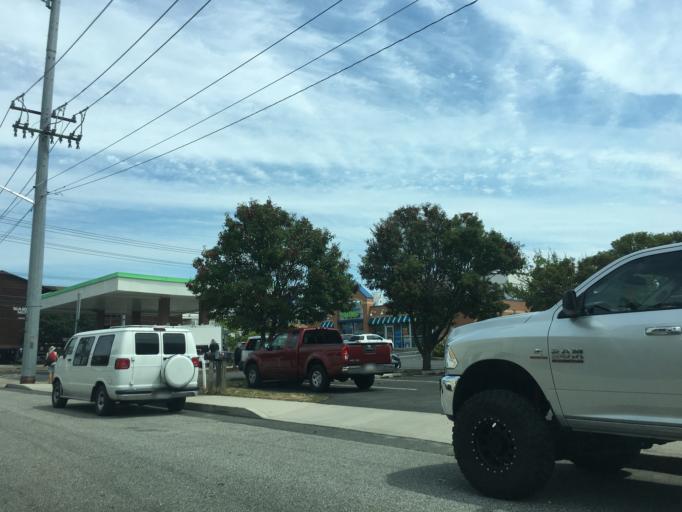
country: US
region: Maryland
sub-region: Worcester County
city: Ocean City
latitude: 38.4028
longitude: -75.0616
